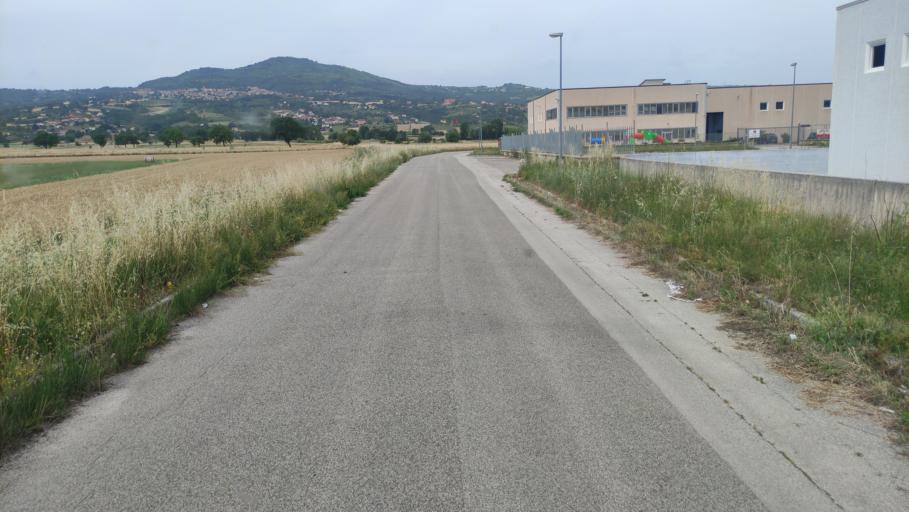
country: IT
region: Campania
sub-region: Provincia di Avellino
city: Sturno
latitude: 41.0460
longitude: 15.1297
